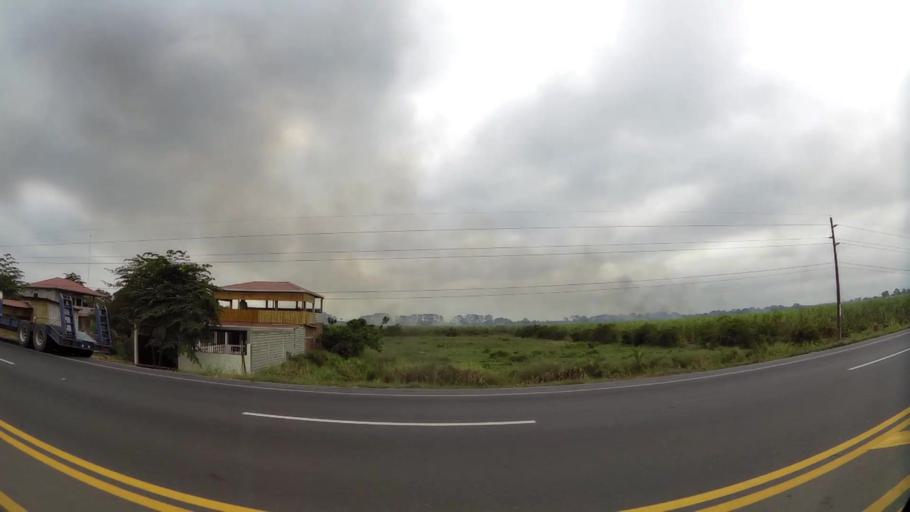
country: EC
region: Guayas
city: Yaguachi Nuevo
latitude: -2.2731
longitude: -79.6383
